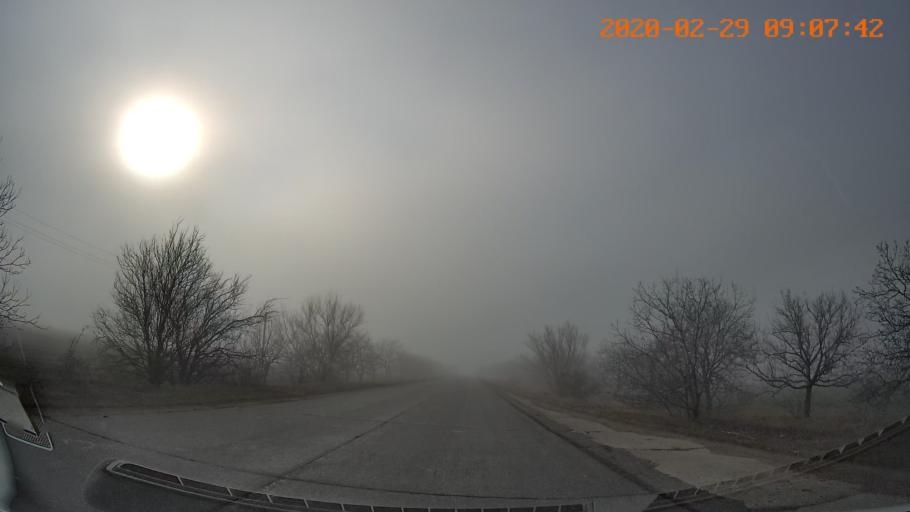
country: MD
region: Telenesti
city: Tiraspolul Nou
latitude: 46.8593
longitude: 29.7497
